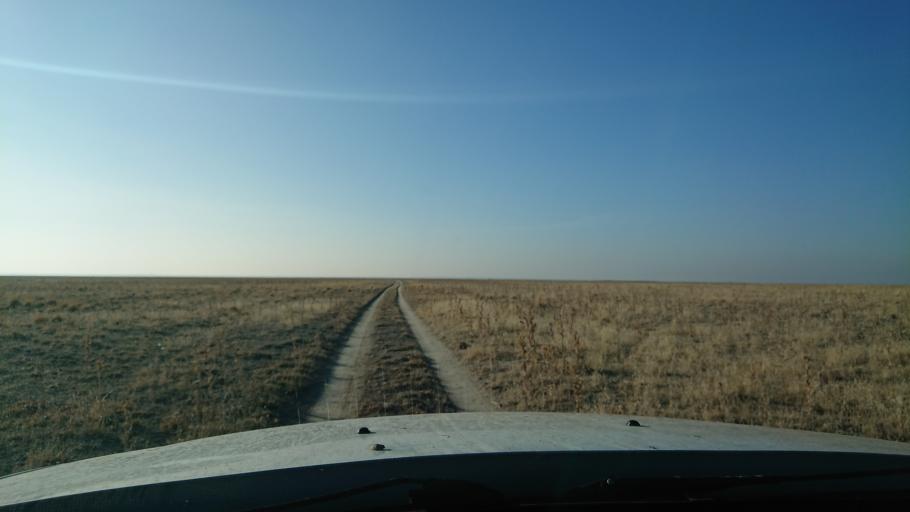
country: TR
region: Aksaray
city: Sultanhani
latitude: 38.3713
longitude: 33.5544
